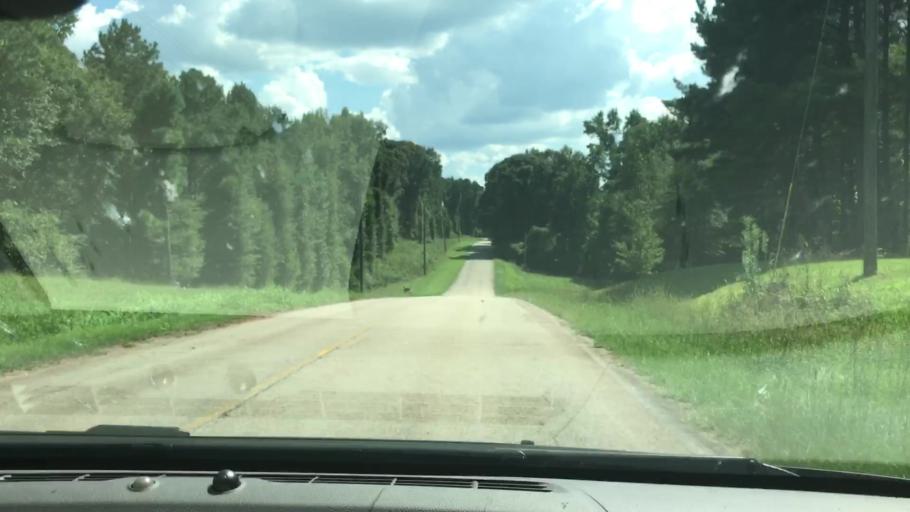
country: US
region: Georgia
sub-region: Troup County
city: La Grange
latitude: 33.0970
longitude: -85.1298
